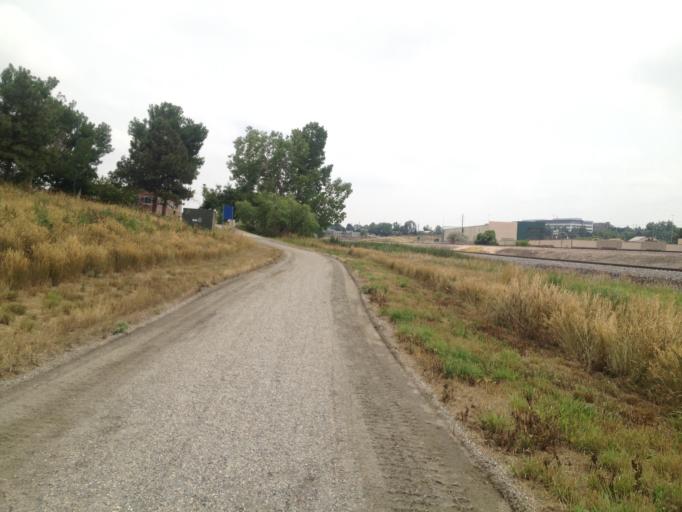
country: US
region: Colorado
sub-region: Broomfield County
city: Broomfield
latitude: 39.9266
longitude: -105.1097
